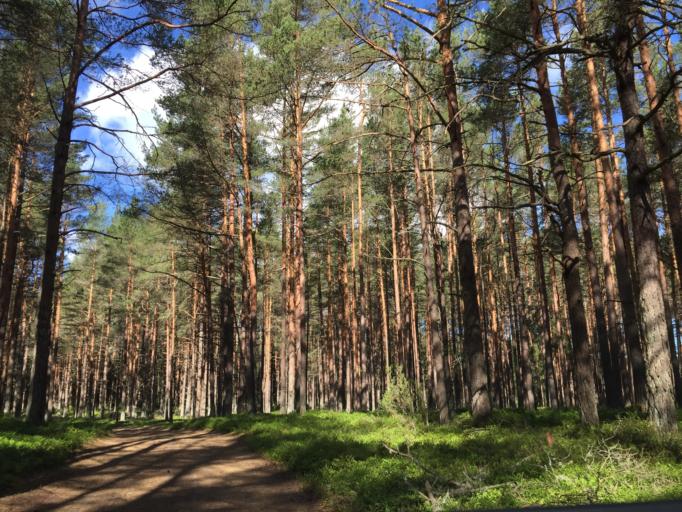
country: LV
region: Ventspils
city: Ventspils
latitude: 57.4647
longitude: 21.6329
